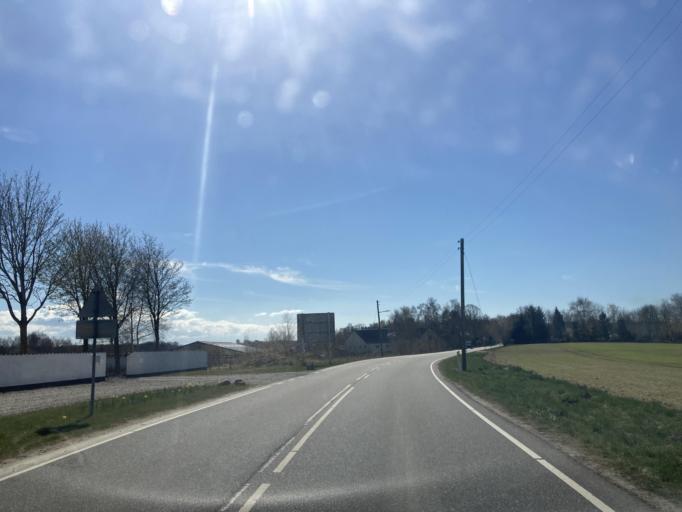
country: DK
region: Capital Region
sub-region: Gribskov Kommune
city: Graested
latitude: 56.0251
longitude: 12.2786
